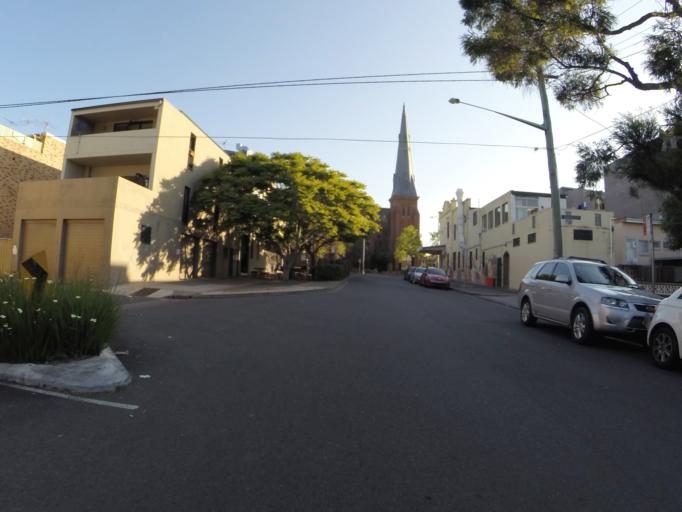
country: AU
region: New South Wales
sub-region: Marrickville
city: Marrickville
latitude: -33.9092
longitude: 151.1552
